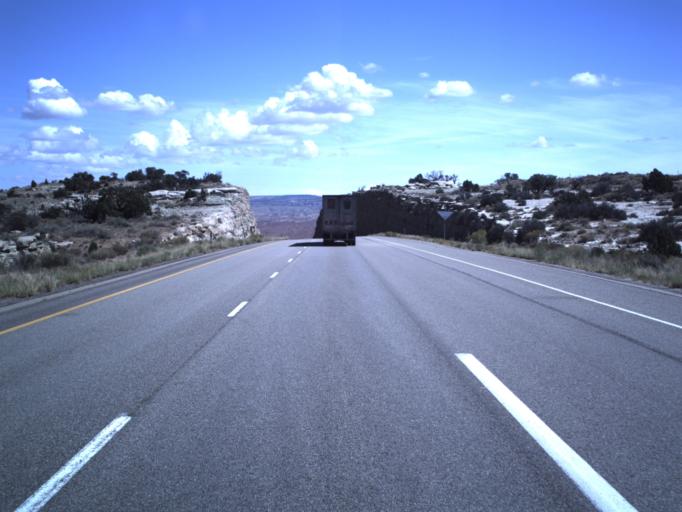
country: US
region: Utah
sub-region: Emery County
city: Ferron
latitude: 38.8303
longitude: -111.1176
